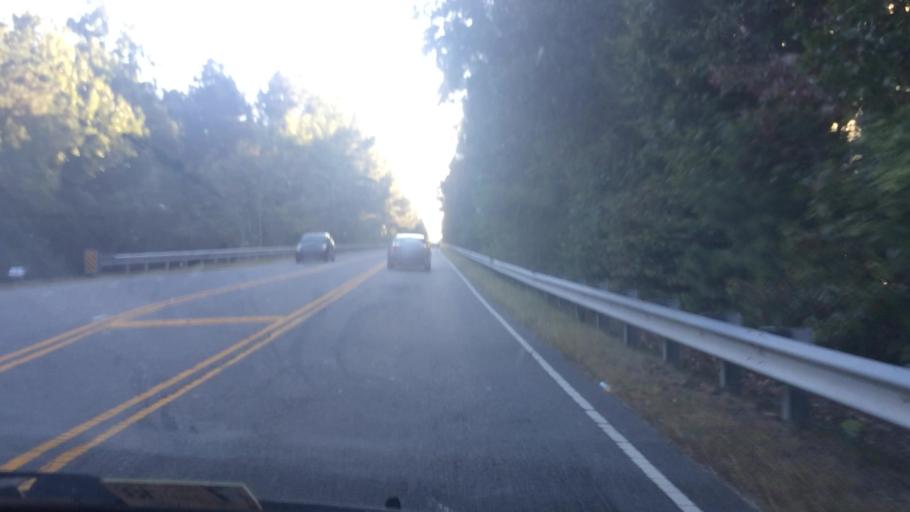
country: US
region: Virginia
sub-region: James City County
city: Williamsburg
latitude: 37.3785
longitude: -76.7709
